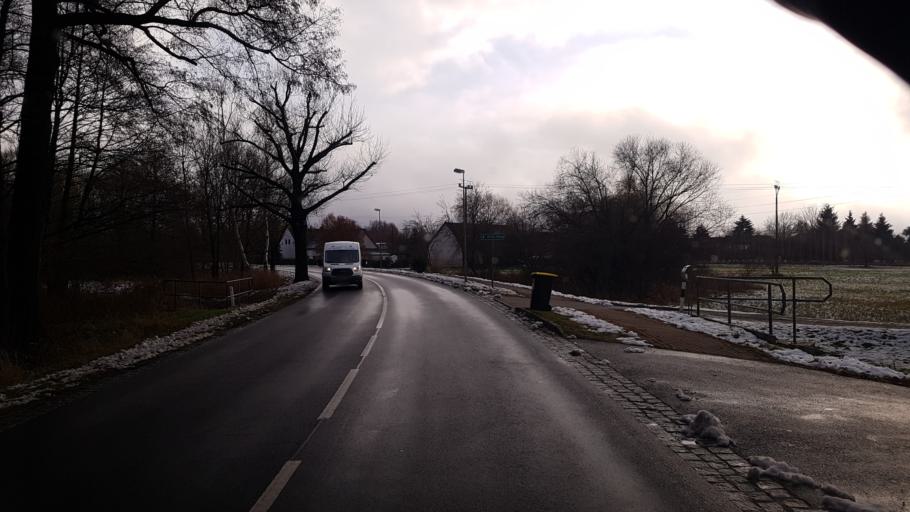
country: DE
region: Brandenburg
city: Forst
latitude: 51.8058
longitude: 14.6005
